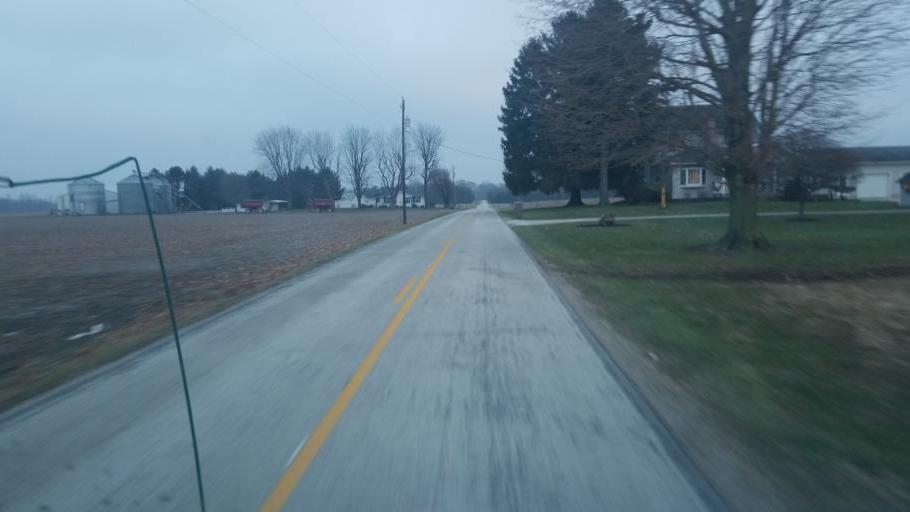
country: US
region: Ohio
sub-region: Seneca County
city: Tiffin
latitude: 40.9929
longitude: -83.2163
